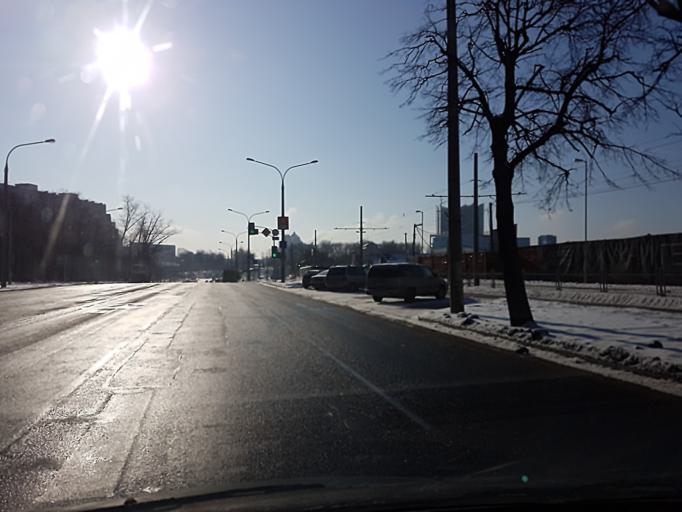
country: BY
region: Minsk
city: Minsk
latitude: 53.9214
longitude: 27.5494
